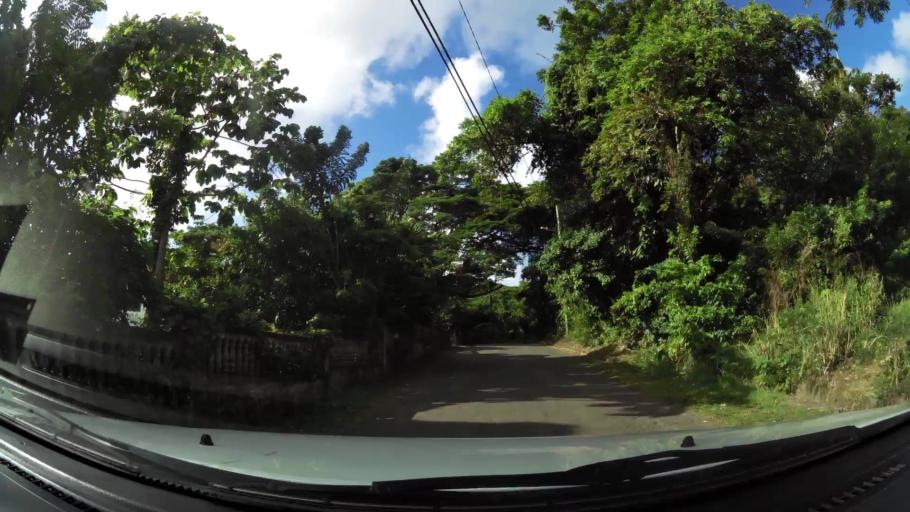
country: LC
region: Gros-Islet
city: Gros Islet
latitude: 14.0468
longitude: -60.9618
